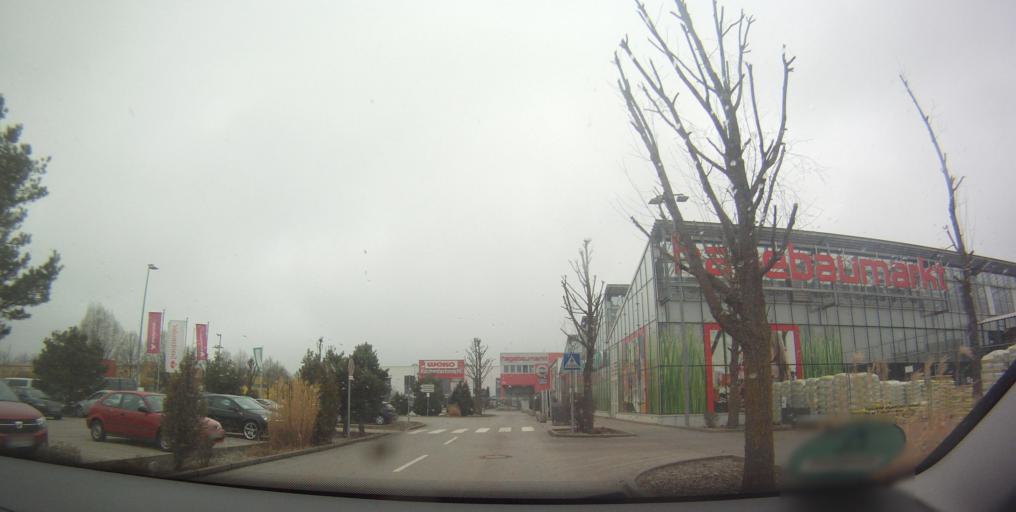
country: DE
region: Bavaria
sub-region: Upper Bavaria
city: Eching
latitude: 48.3065
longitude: 11.6340
